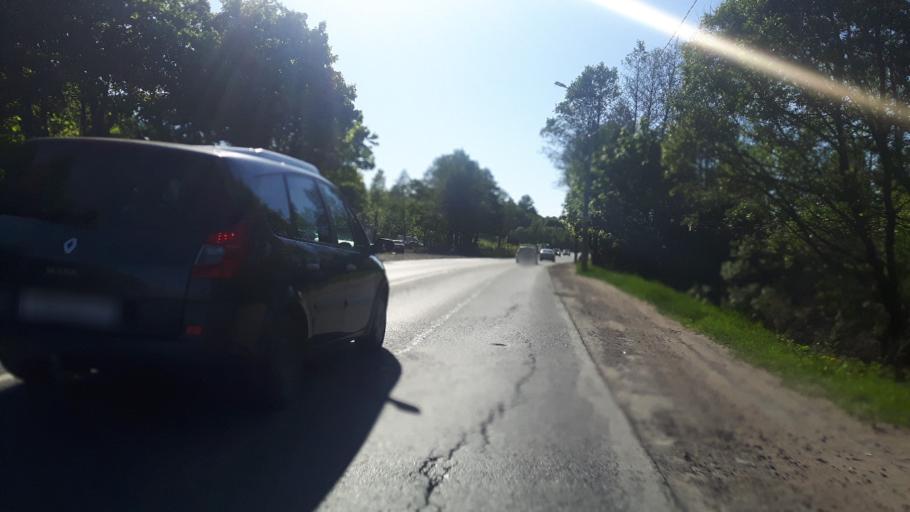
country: RU
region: St.-Petersburg
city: Bol'shaya Izhora
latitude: 59.9269
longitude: 29.6615
